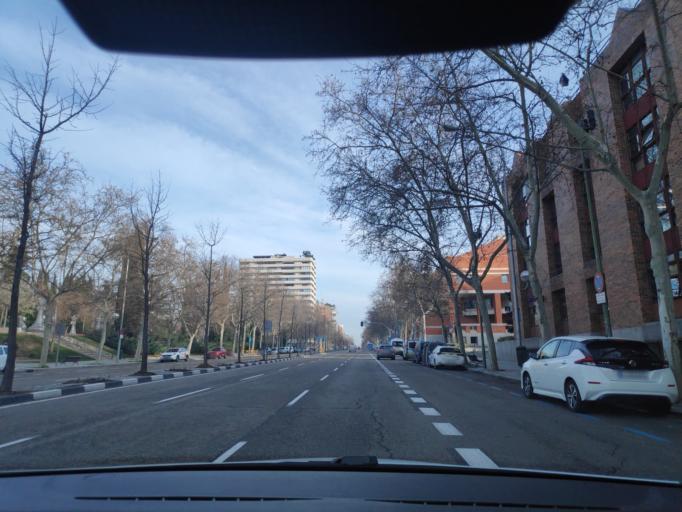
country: ES
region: Madrid
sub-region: Provincia de Madrid
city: Salamanca
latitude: 40.4447
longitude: -3.6782
